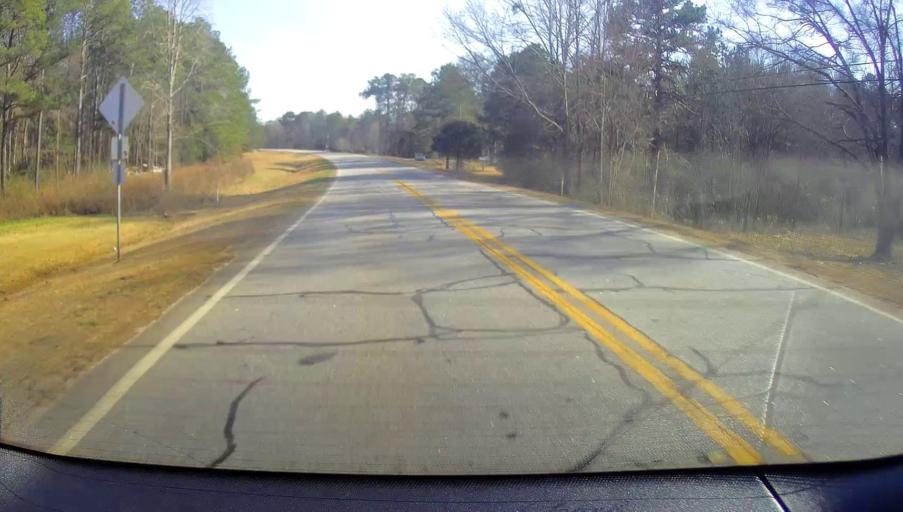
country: US
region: Georgia
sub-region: Butts County
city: Indian Springs
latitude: 33.2531
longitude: -83.8978
